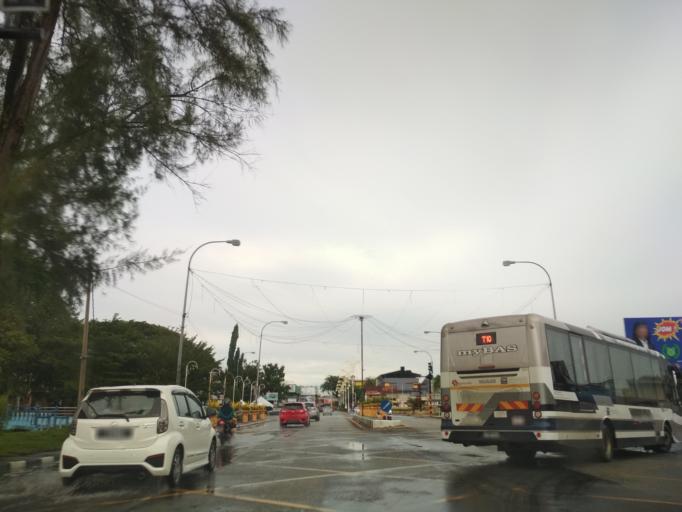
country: MY
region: Perlis
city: Kangar
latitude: 6.4370
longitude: 100.1906
